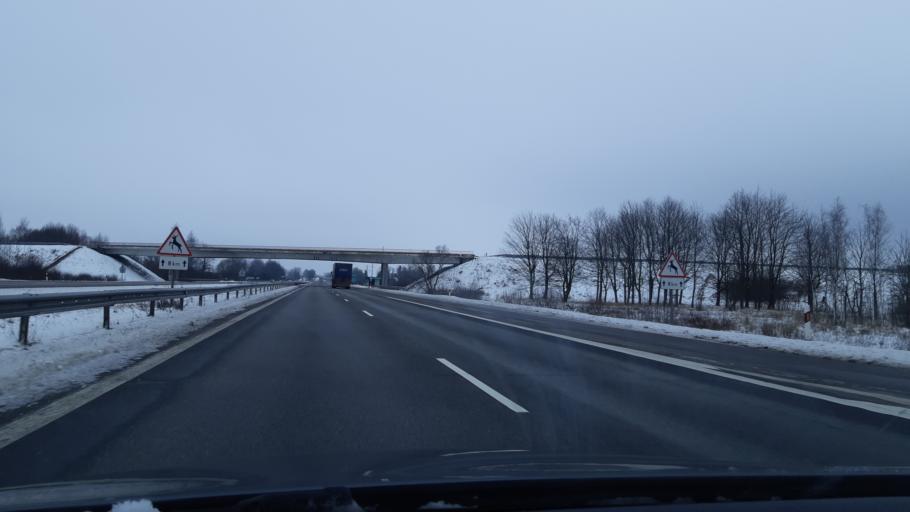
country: LT
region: Kauno apskritis
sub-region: Kaunas
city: Sargenai
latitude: 55.0368
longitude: 23.8250
